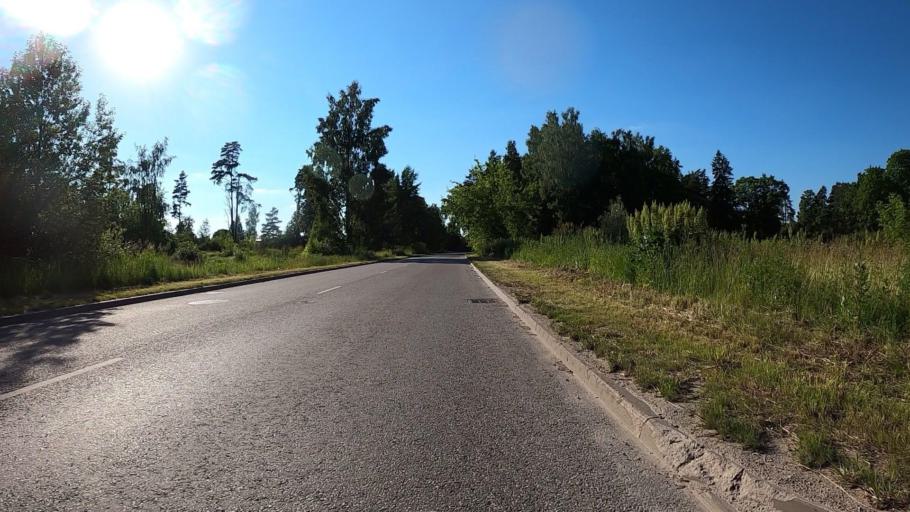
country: LV
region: Kekava
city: Kekava
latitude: 56.8868
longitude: 24.2508
